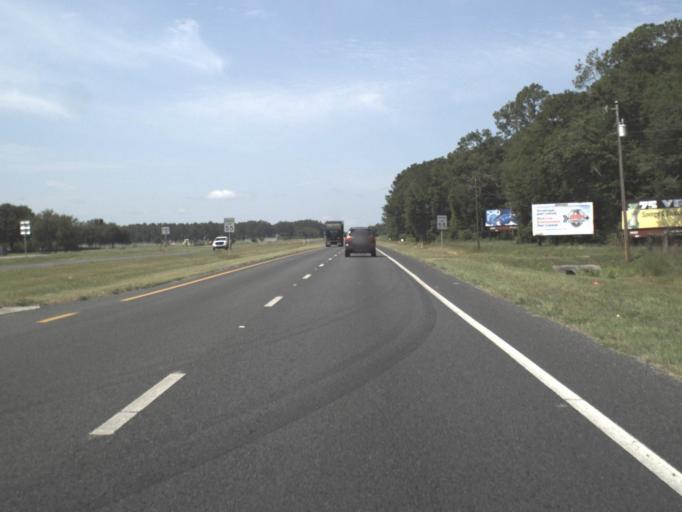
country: US
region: Florida
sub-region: Alachua County
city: Gainesville
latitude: 29.6969
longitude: -82.2813
